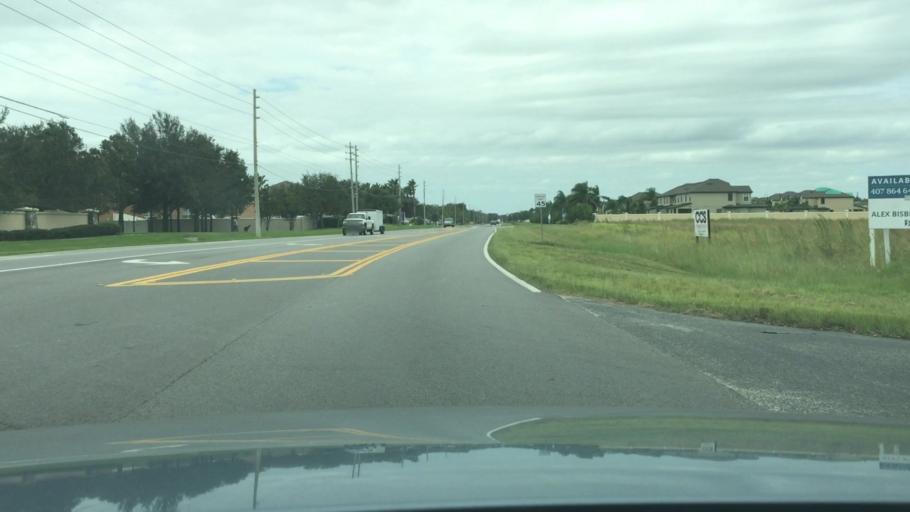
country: US
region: Florida
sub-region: Osceola County
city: Saint Cloud
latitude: 28.1992
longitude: -81.2961
